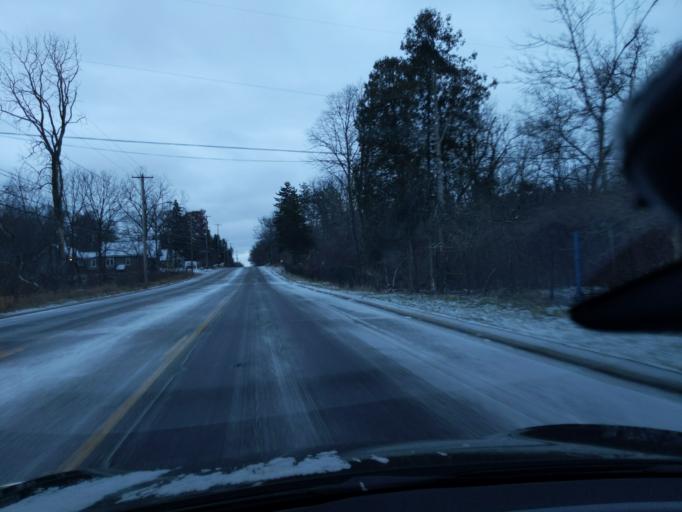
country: US
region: Michigan
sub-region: Ingham County
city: Lansing
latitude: 42.7118
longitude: -84.5193
